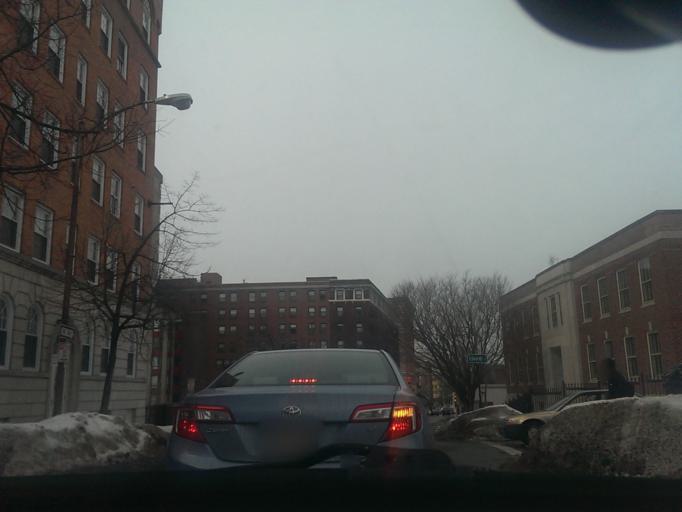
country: US
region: Massachusetts
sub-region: Hampden County
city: Springfield
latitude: 42.1040
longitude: -72.5872
